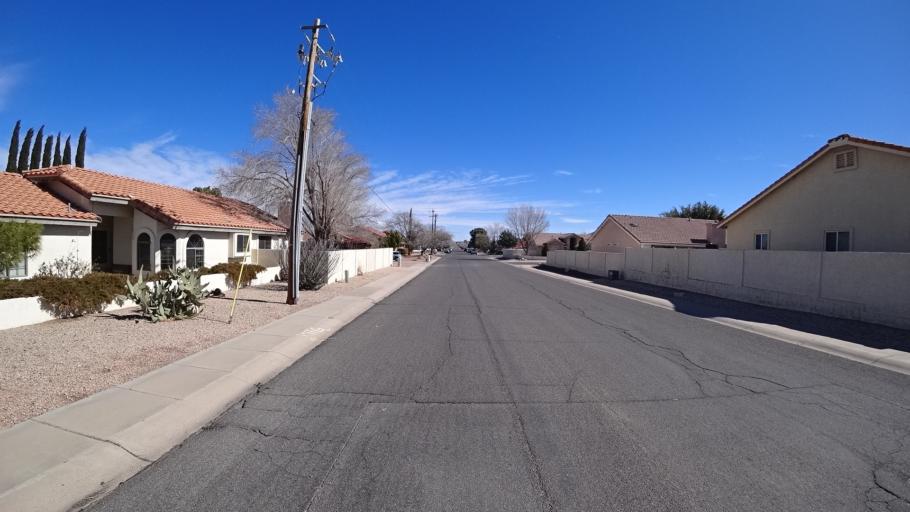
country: US
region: Arizona
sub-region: Mohave County
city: Kingman
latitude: 35.2104
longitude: -114.0412
